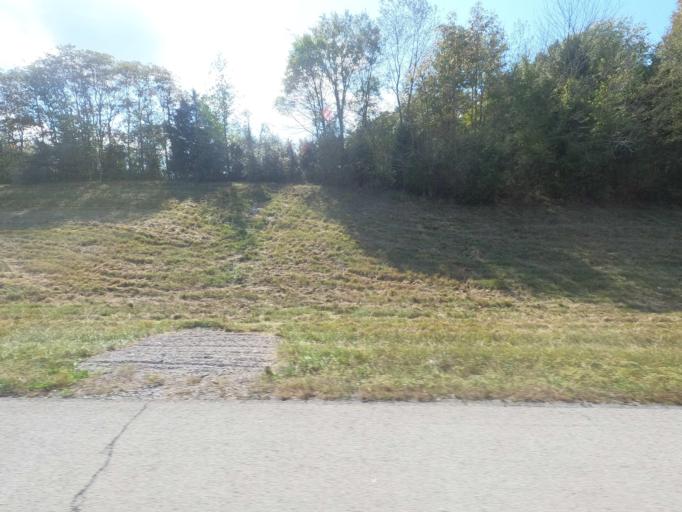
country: US
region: Illinois
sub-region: Johnson County
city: Vienna
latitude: 37.3671
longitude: -88.8047
